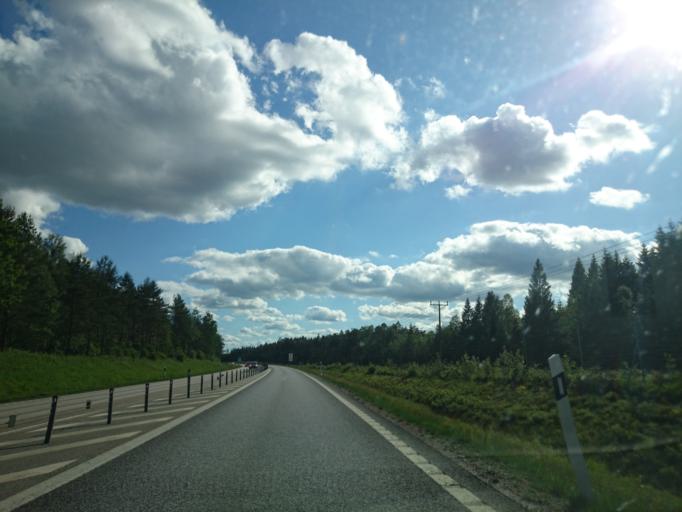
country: SE
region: Kronoberg
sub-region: Ljungby Kommun
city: Ljungby
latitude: 56.8396
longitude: 13.9168
